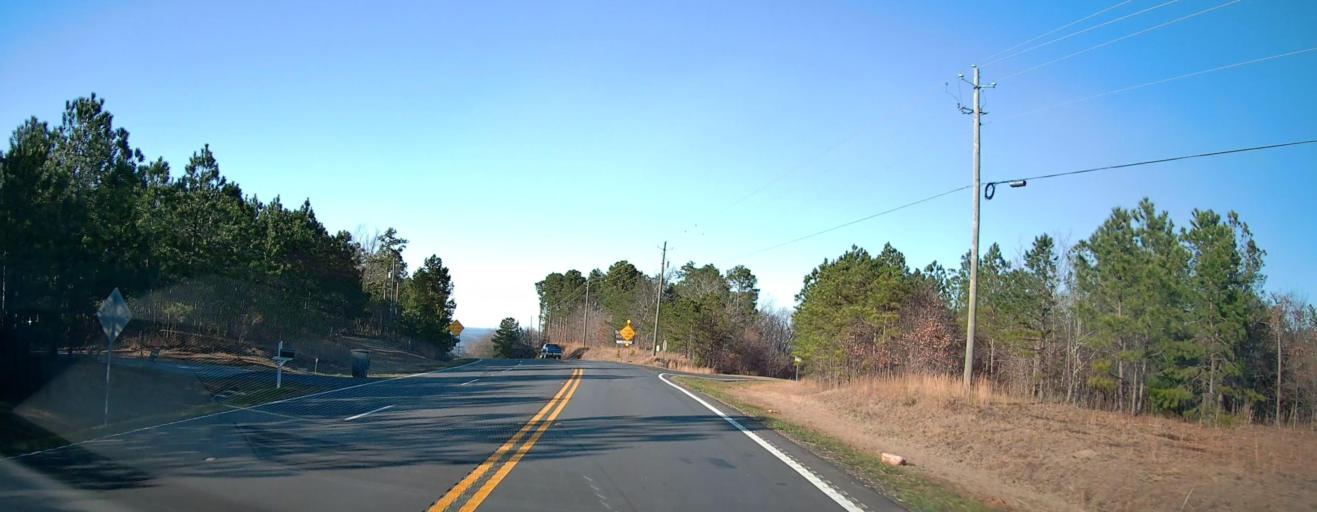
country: US
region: Georgia
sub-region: Meriwether County
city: Manchester
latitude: 32.8723
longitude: -84.6772
